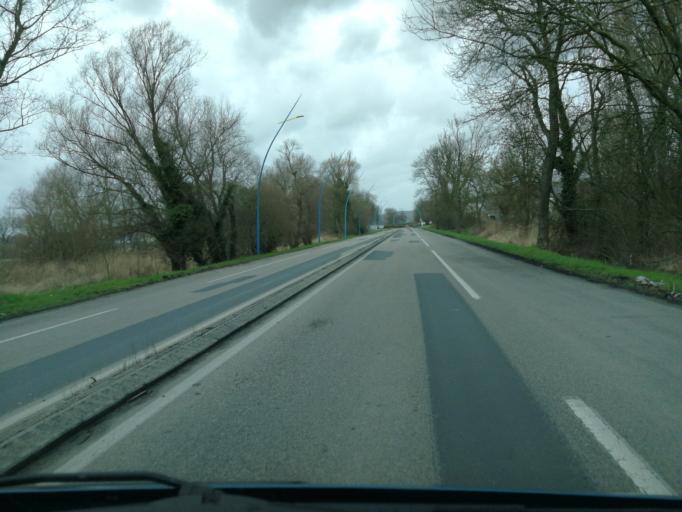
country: FR
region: Haute-Normandie
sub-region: Departement de l'Eure
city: Quillebeuf-sur-Seine
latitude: 49.4827
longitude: 0.5330
